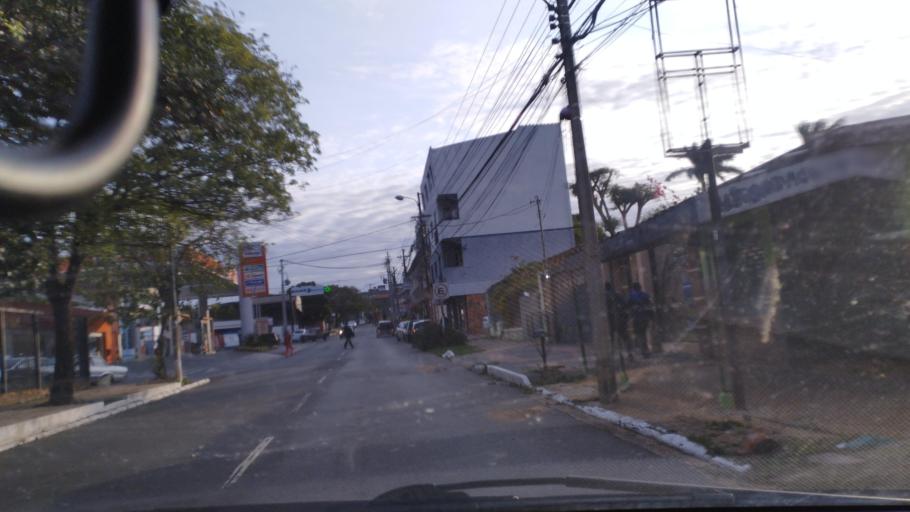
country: PY
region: Central
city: Fernando de la Mora
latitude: -25.3198
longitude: -57.5513
